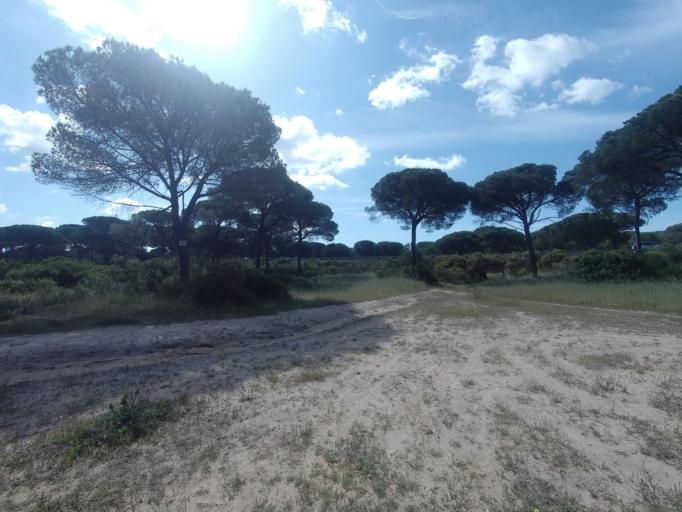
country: ES
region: Andalusia
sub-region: Provincia de Huelva
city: Aljaraque
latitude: 37.2345
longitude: -7.0603
